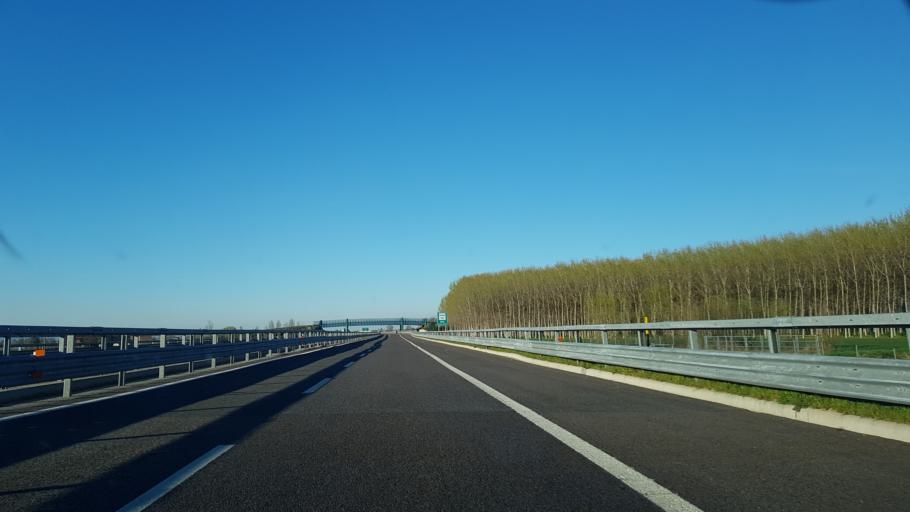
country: IT
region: Veneto
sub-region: Provincia di Padova
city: Megliadino San Vitale
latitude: 45.1880
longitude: 11.5407
